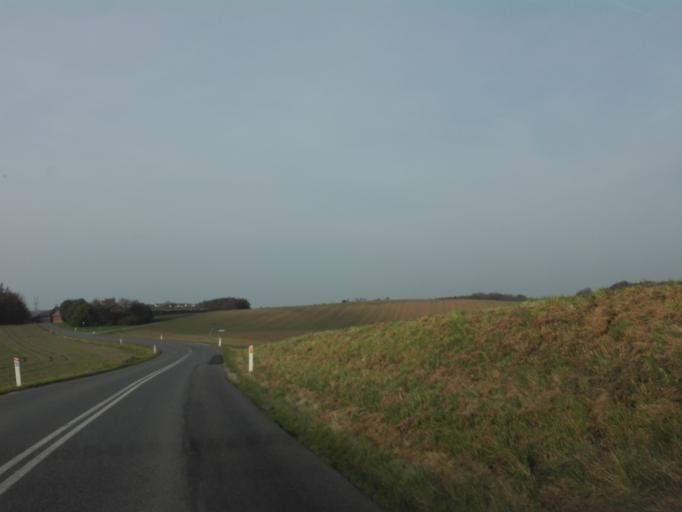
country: DK
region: Central Jutland
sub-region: Odder Kommune
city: Odder
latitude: 55.9934
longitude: 10.1224
